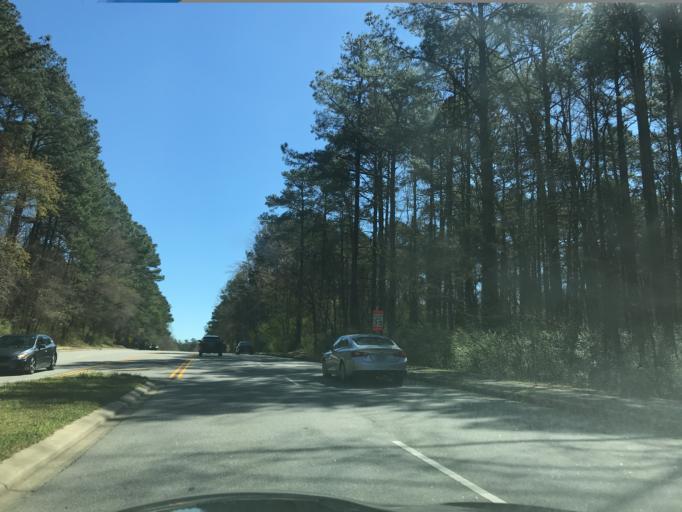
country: US
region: North Carolina
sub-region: Wake County
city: Garner
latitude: 35.6866
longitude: -78.6299
